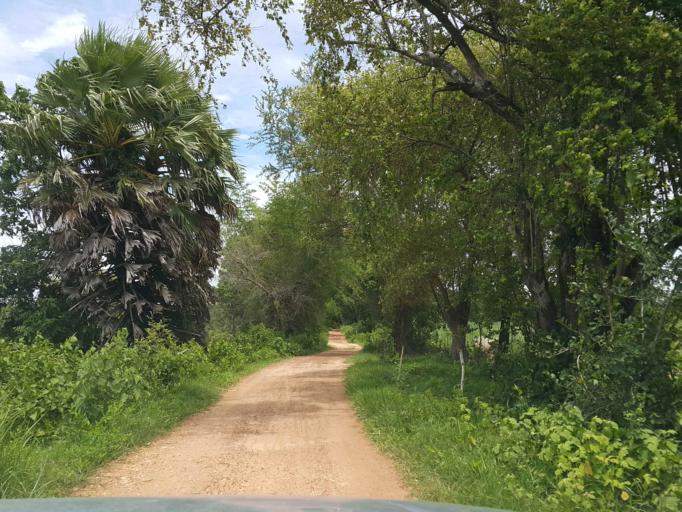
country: TH
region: Sukhothai
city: Ban Na
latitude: 17.0044
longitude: 99.6978
